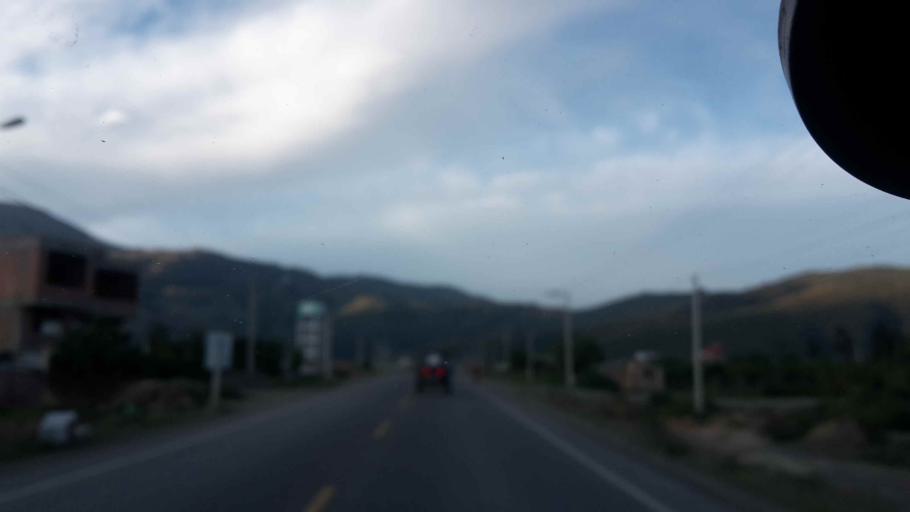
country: BO
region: Cochabamba
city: Punata
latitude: -17.5291
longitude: -65.8350
